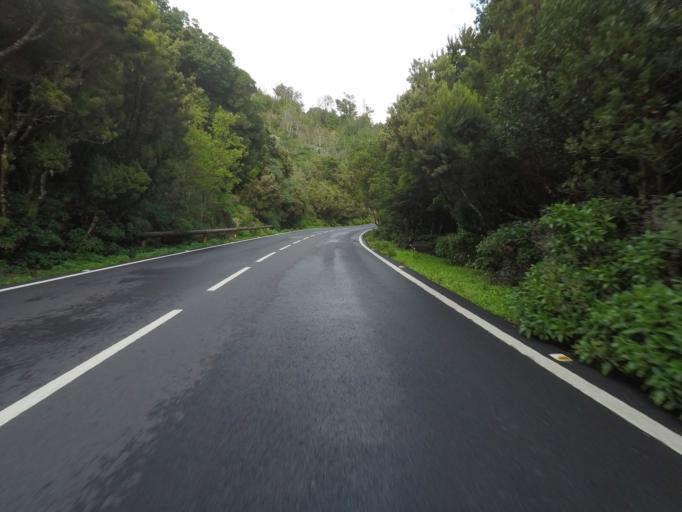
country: ES
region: Canary Islands
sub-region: Provincia de Santa Cruz de Tenerife
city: Alajero
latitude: 28.1099
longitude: -17.2170
